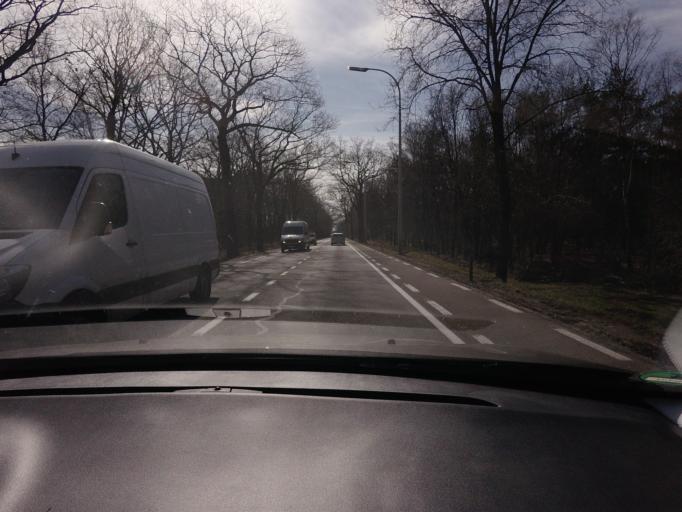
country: BE
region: Flanders
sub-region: Provincie Limburg
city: Helchteren
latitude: 51.0867
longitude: 5.3774
